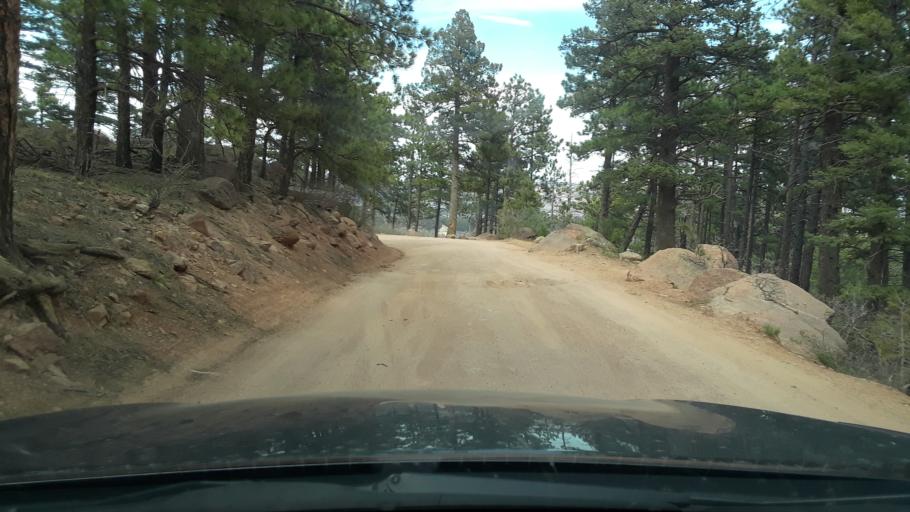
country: US
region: Colorado
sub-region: El Paso County
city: Palmer Lake
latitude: 39.0754
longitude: -104.9171
